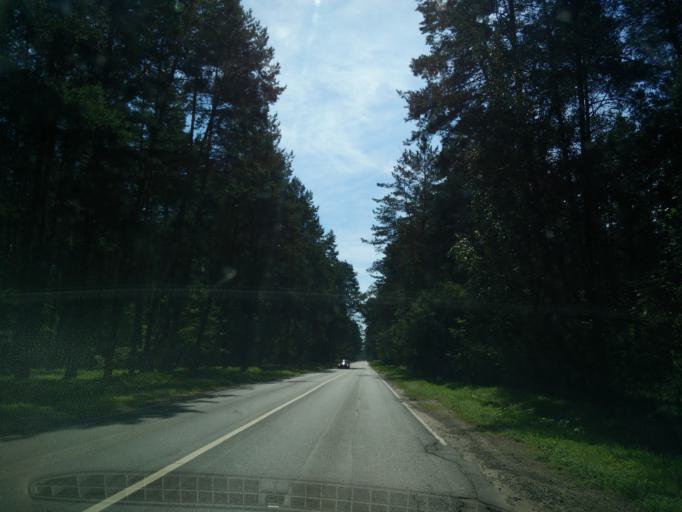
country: LT
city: Nemencine
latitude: 54.7850
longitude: 25.3836
